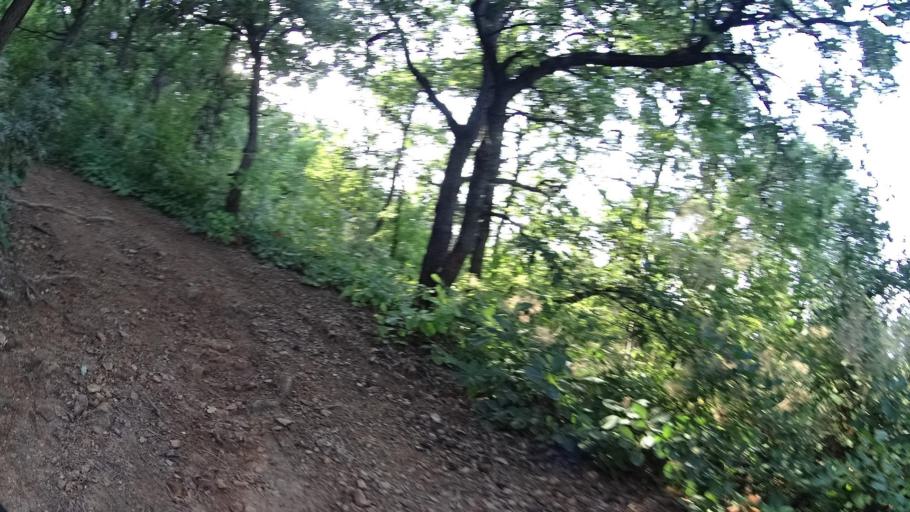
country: BG
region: Plovdiv
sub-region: Obshtina Plovdiv
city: Plovdiv
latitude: 42.0598
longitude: 24.6893
